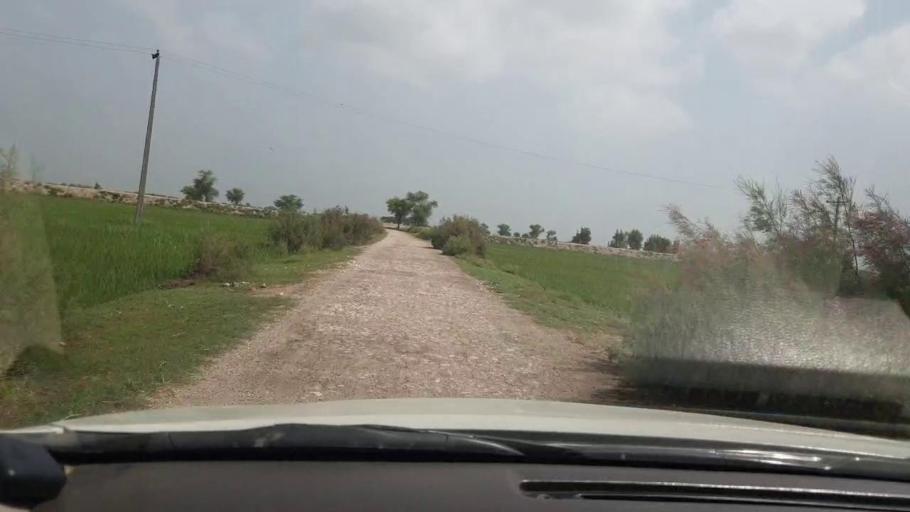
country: PK
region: Sindh
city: Garhi Yasin
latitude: 28.0116
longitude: 68.5400
